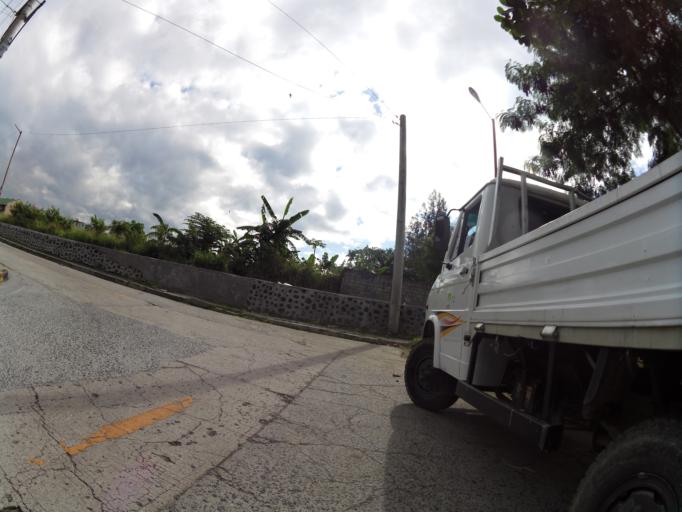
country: PH
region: Metro Manila
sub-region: Marikina
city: Calumpang
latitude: 14.6403
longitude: 121.1043
